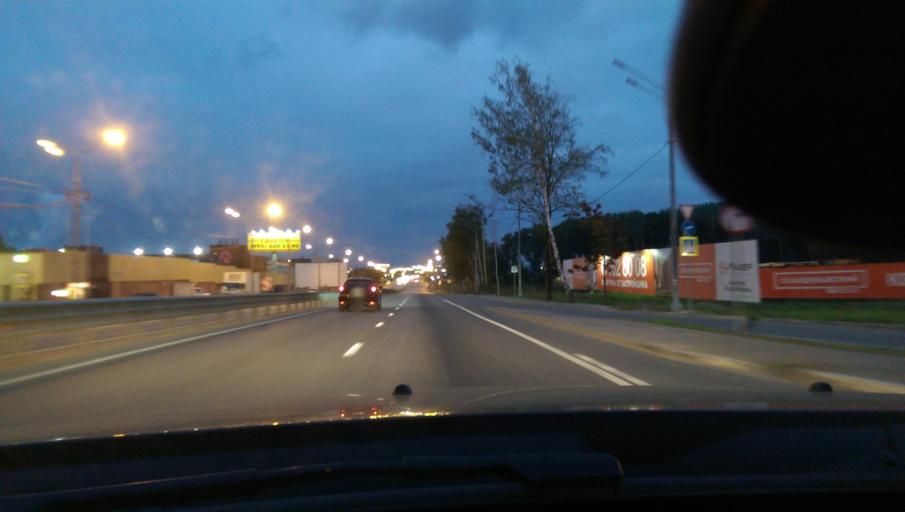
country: RU
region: Moscow
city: Vatutino
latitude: 55.9212
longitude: 37.6641
